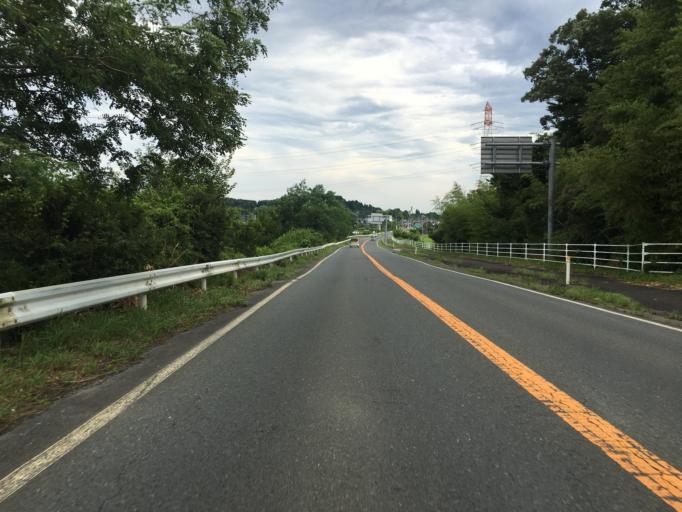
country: JP
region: Miyagi
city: Marumori
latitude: 37.8475
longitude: 140.9166
